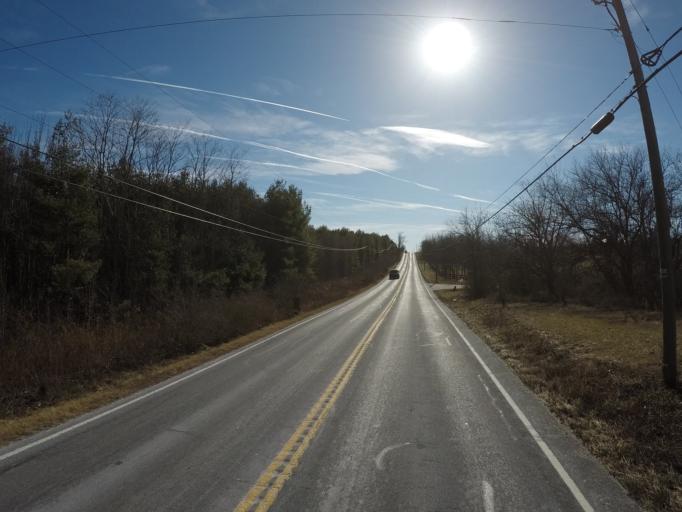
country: US
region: Maryland
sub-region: Frederick County
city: Point of Rocks
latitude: 39.2443
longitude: -77.5309
